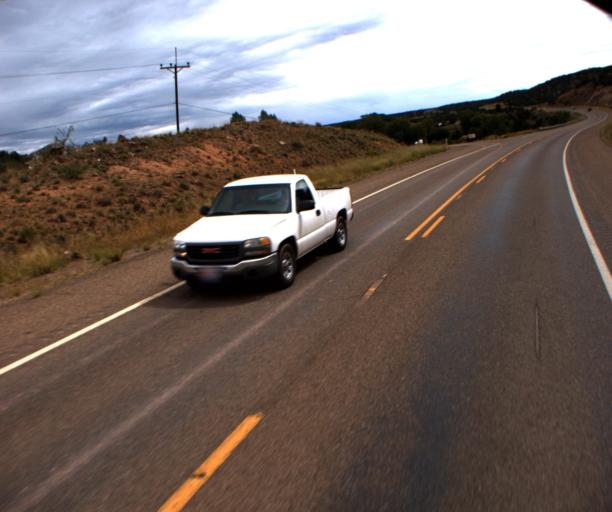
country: US
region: Arizona
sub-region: Navajo County
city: Taylor
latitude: 34.3940
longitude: -110.0654
